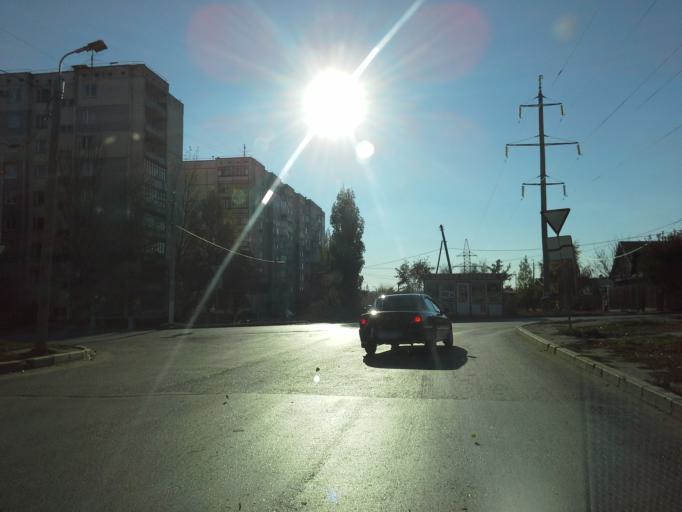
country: RU
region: Volgograd
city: Vodstroy
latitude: 48.8195
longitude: 44.6167
